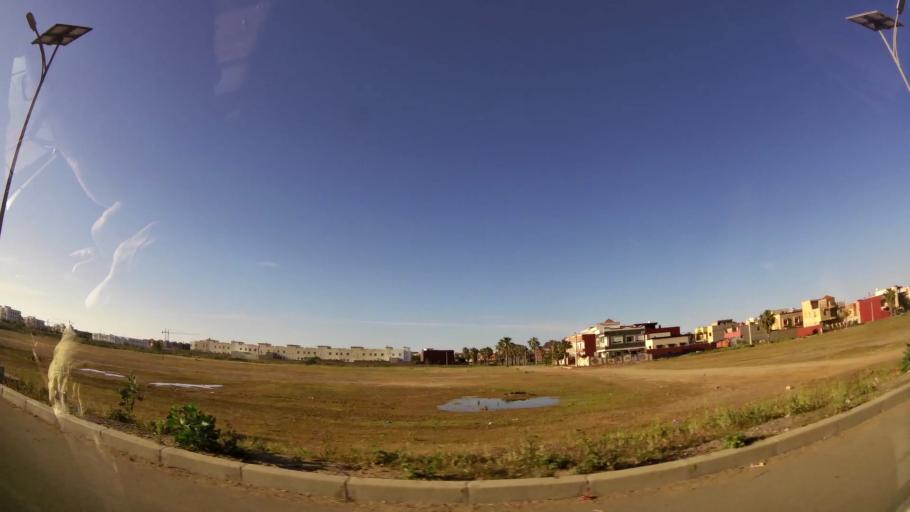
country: MA
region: Oriental
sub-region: Berkane-Taourirt
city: Madagh
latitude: 35.0823
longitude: -2.2500
